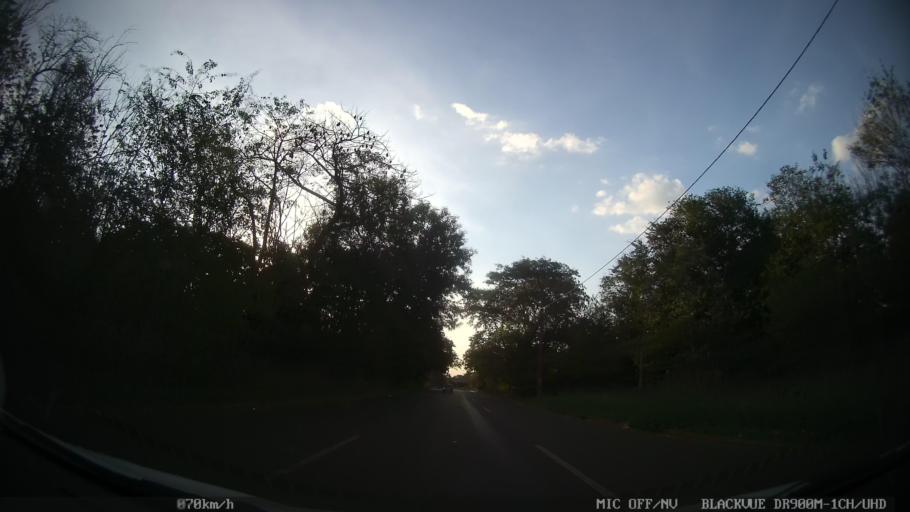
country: BR
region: Sao Paulo
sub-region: Ribeirao Preto
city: Ribeirao Preto
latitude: -21.1105
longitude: -47.8081
